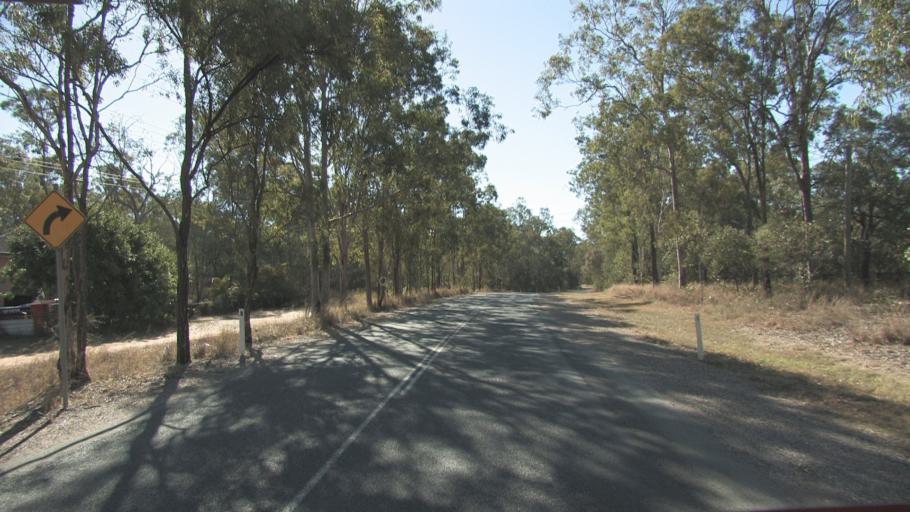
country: AU
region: Queensland
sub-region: Logan
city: North Maclean
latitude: -27.7581
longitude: 152.9955
